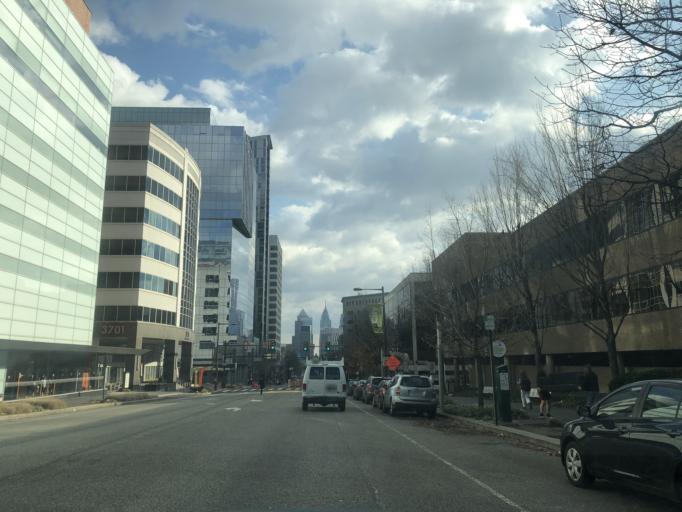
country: US
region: Pennsylvania
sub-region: Philadelphia County
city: Philadelphia
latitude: 39.9565
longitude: -75.1972
